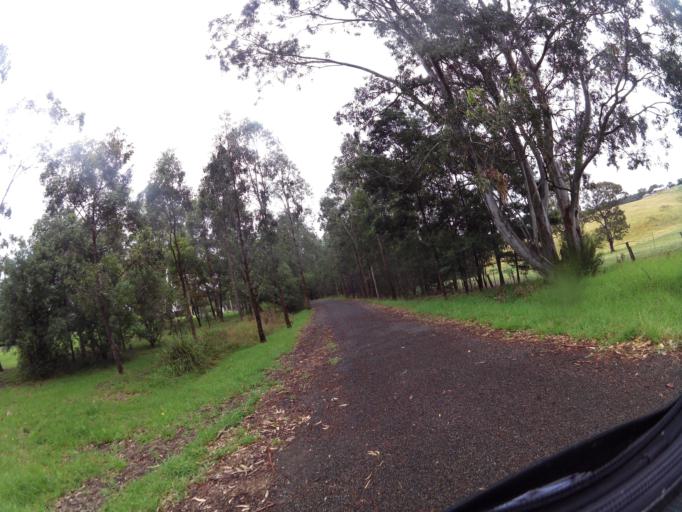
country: AU
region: Victoria
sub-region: East Gippsland
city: Bairnsdale
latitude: -37.8144
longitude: 147.7341
